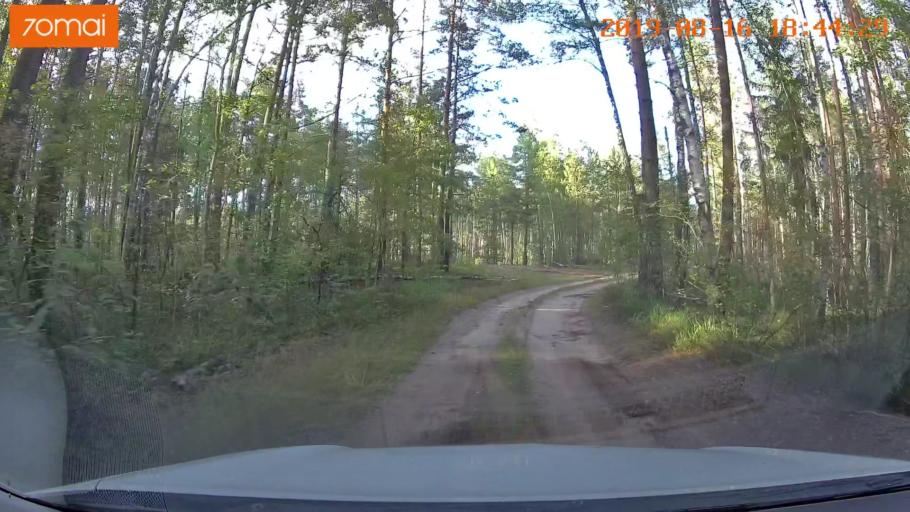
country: BY
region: Mogilev
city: Asipovichy
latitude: 53.2213
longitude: 28.6559
